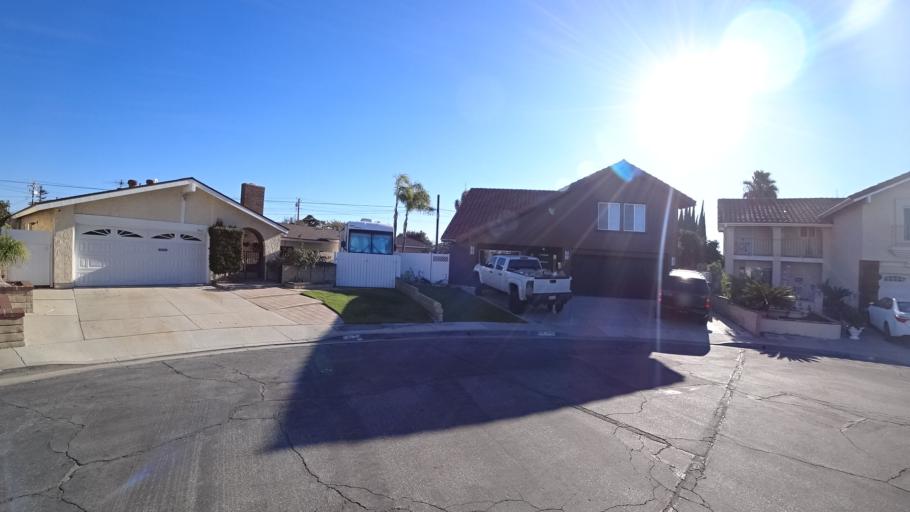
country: US
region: California
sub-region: Orange County
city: Garden Grove
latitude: 33.7680
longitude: -117.9642
